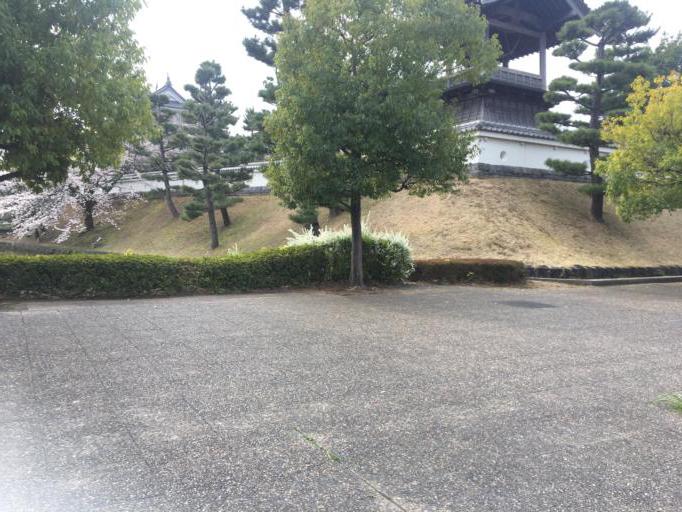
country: JP
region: Saitama
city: Gyoda
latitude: 36.1387
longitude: 139.4537
